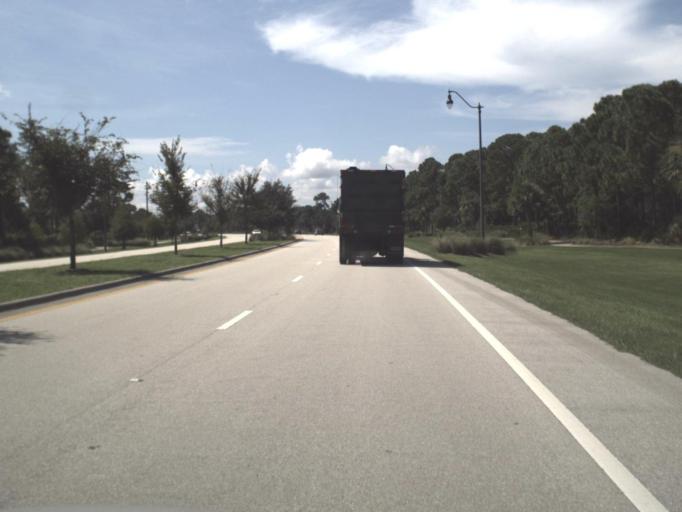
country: US
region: Florida
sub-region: Sarasota County
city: North Port
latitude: 27.0414
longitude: -82.1622
